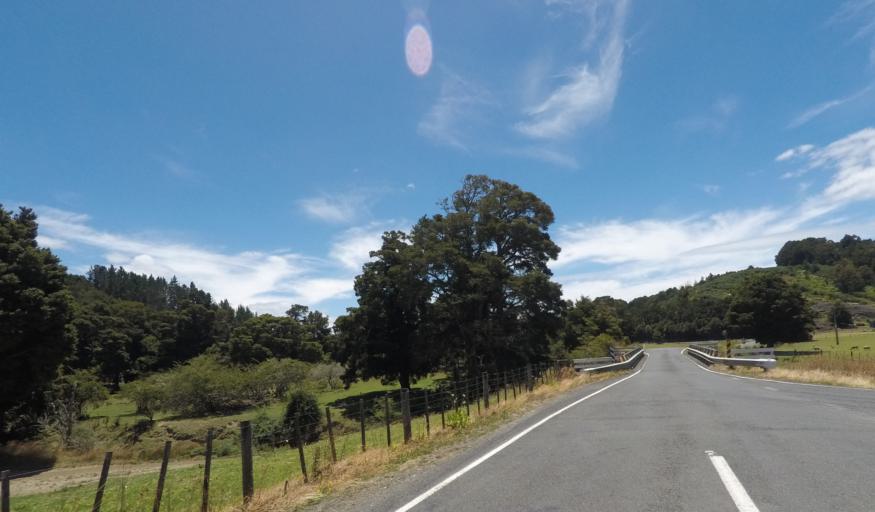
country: NZ
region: Northland
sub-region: Whangarei
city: Whangarei
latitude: -35.5424
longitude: 174.3085
